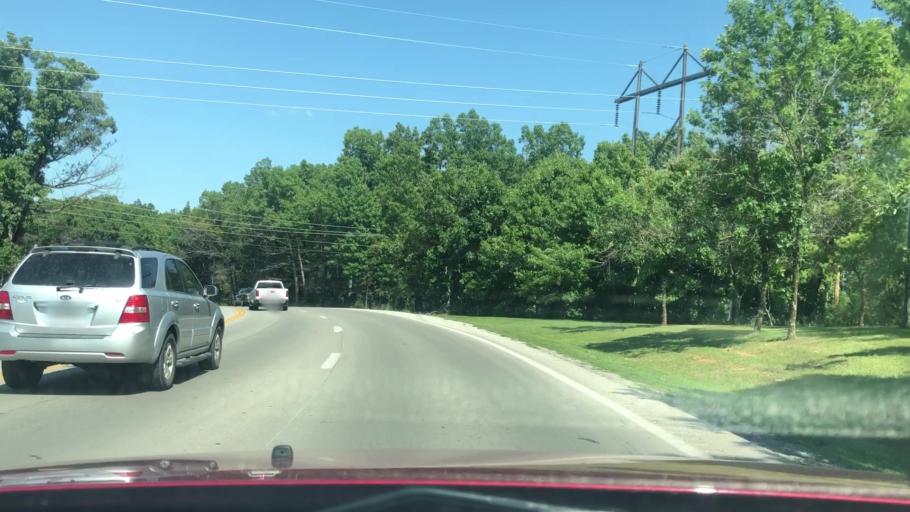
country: US
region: Missouri
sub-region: Stone County
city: Kimberling City
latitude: 36.6711
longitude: -93.3344
